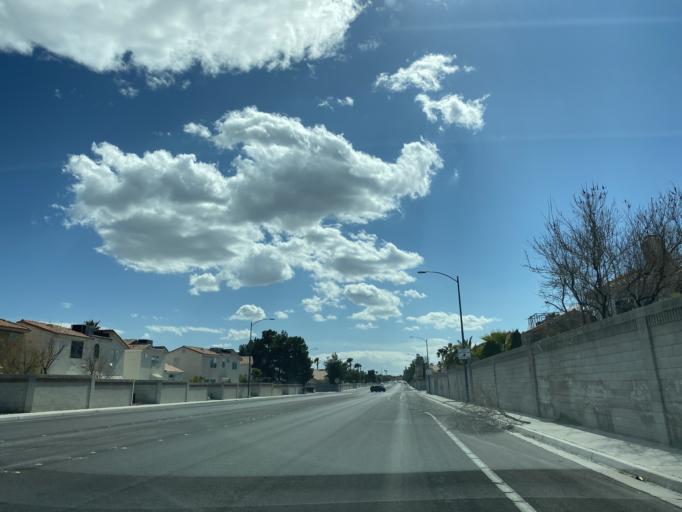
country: US
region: Nevada
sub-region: Clark County
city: Summerlin South
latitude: 36.2275
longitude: -115.2883
